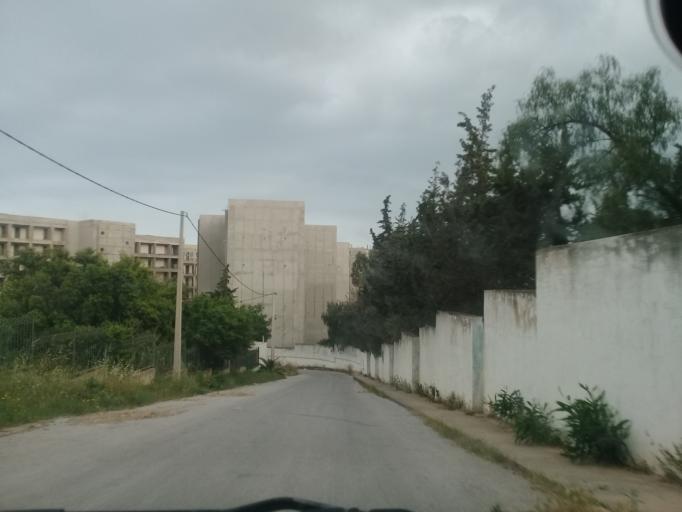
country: TN
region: Tunis
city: Sidi Bou Said
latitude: 36.8657
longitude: 10.3398
